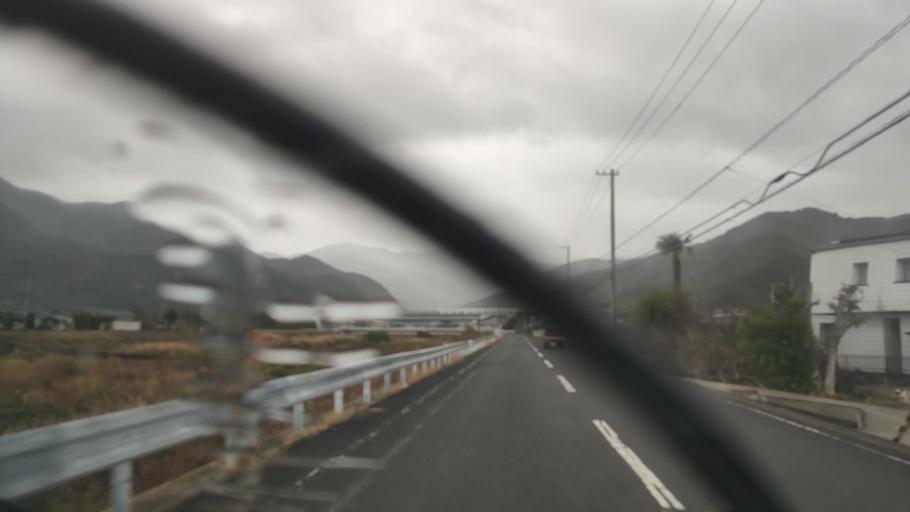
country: JP
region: Tokushima
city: Ishii
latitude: 34.2105
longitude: 134.4047
